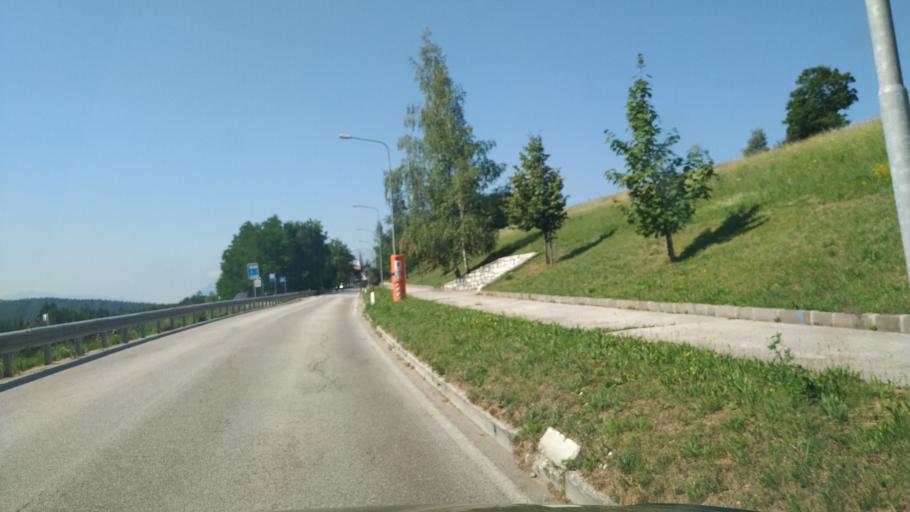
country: IT
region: Trentino-Alto Adige
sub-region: Provincia di Trento
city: Romeno
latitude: 46.4000
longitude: 11.1276
